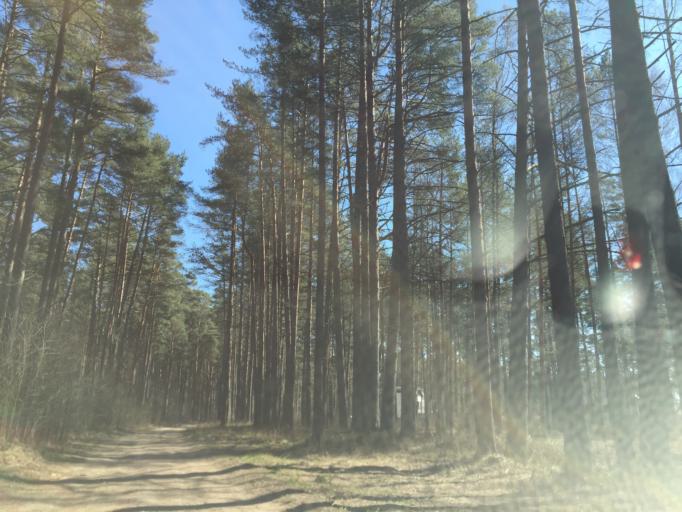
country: LV
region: Jurmala
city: Jurmala
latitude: 56.9454
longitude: 23.7073
